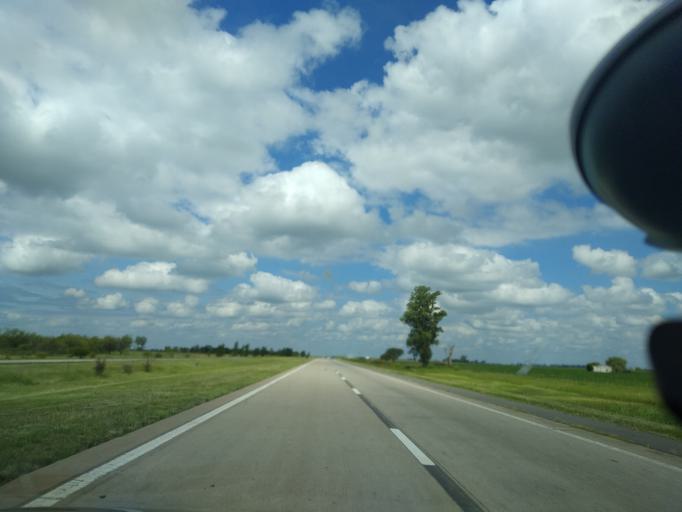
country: AR
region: Cordoba
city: Bell Ville
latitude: -32.5926
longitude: -62.5001
